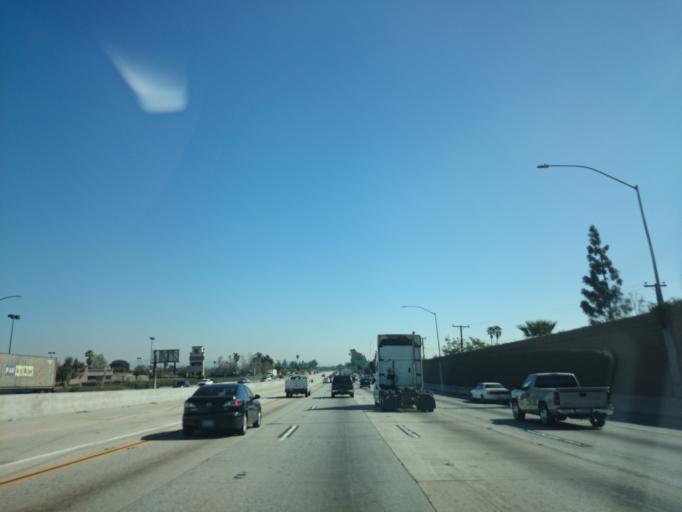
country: US
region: California
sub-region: San Bernardino County
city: Ontario
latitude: 34.0764
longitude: -117.6214
